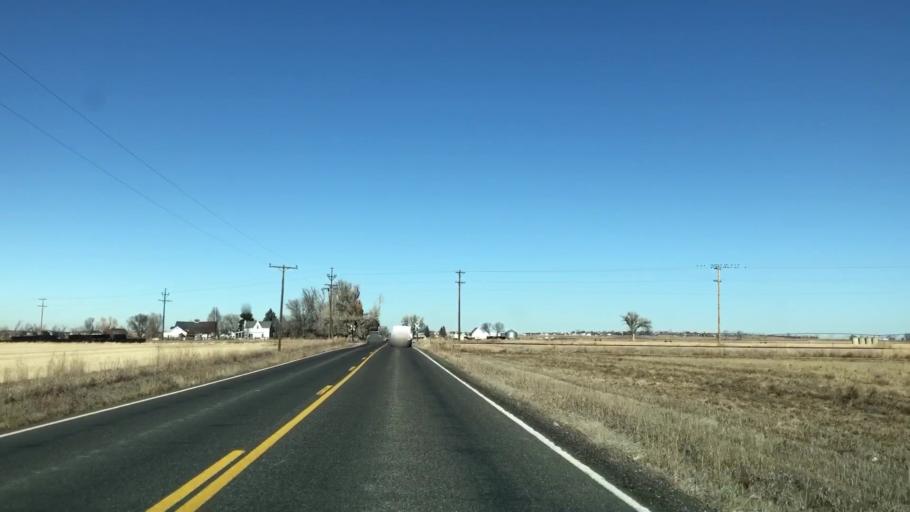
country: US
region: Colorado
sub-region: Weld County
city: Windsor
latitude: 40.5036
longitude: -104.9441
